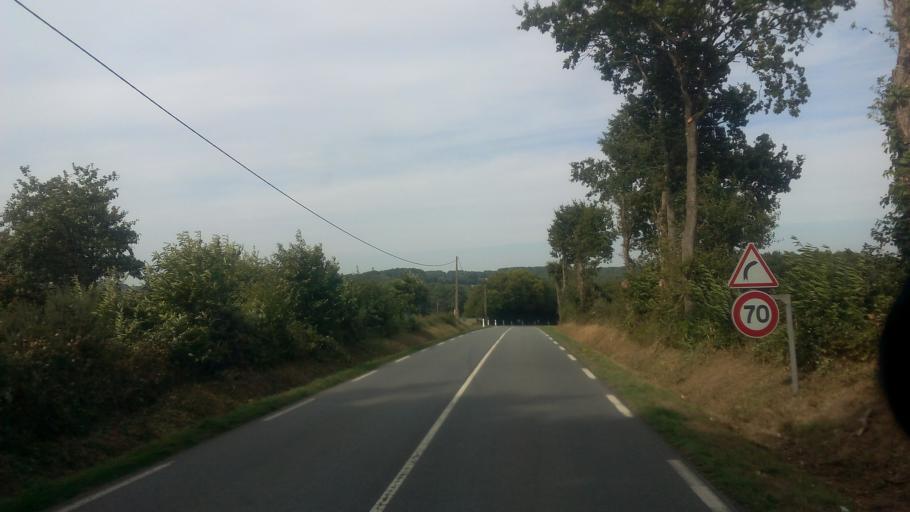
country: FR
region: Brittany
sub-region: Departement d'Ille-et-Vilaine
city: Bains-sur-Oust
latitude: 47.7254
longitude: -2.1039
